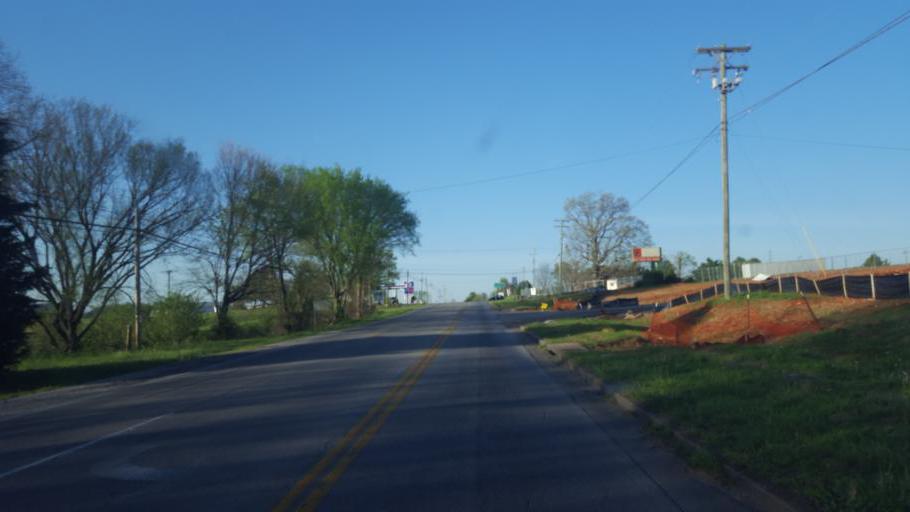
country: US
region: Kentucky
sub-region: Hart County
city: Munfordville
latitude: 37.2595
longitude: -85.8837
